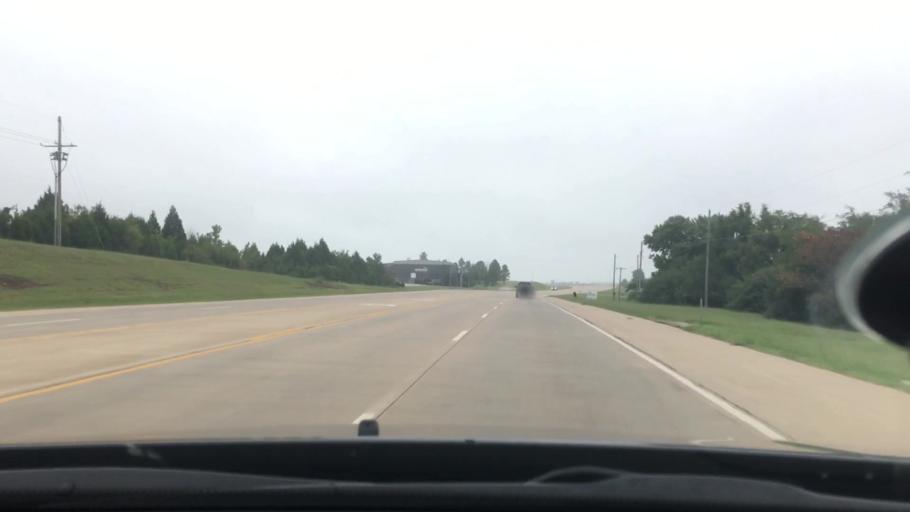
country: US
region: Oklahoma
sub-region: Seminole County
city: Seminole
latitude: 35.2659
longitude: -96.6710
